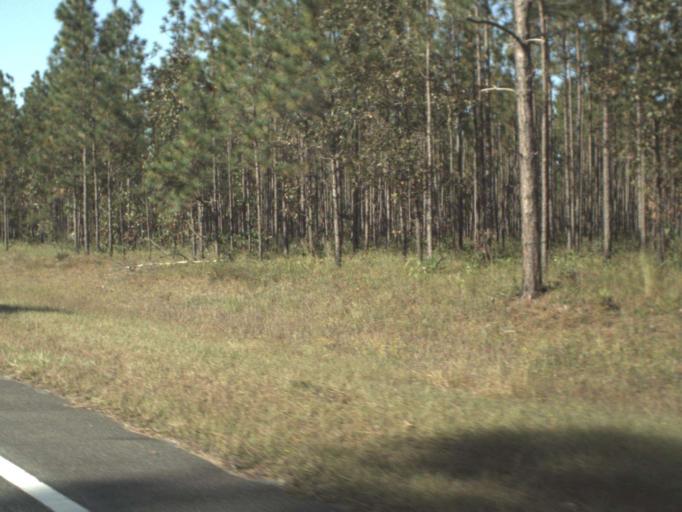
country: US
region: Florida
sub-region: Wakulla County
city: Crawfordville
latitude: 30.2950
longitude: -84.4108
